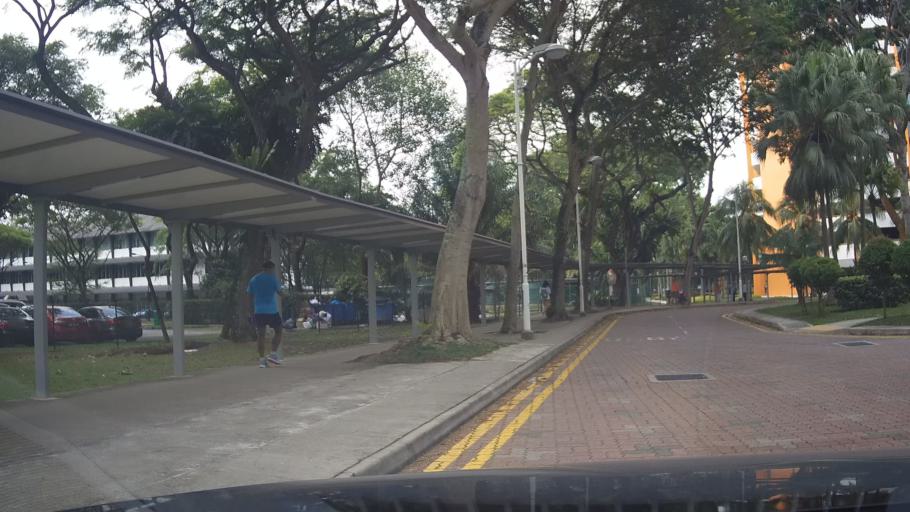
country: SG
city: Singapore
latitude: 1.3076
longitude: 103.8822
